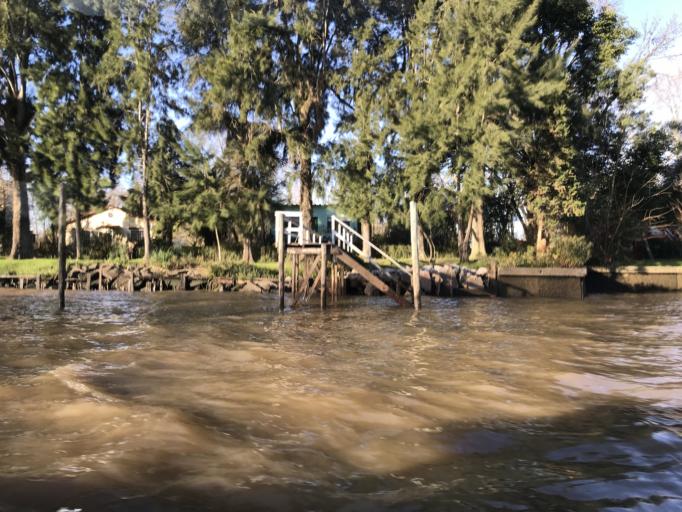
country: AR
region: Buenos Aires
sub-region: Partido de Tigre
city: Tigre
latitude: -34.4016
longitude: -58.5944
